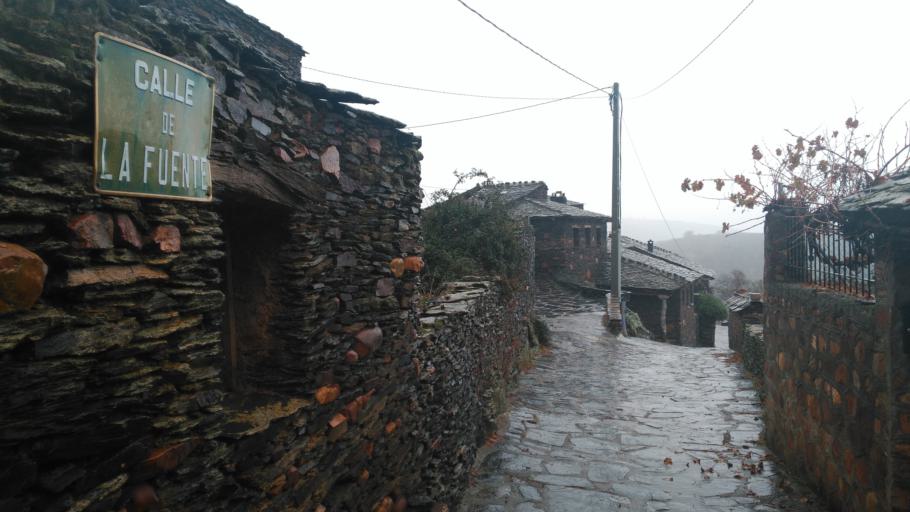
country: ES
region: Castille-La Mancha
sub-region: Provincia de Guadalajara
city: Campillo de Ranas
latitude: 41.0739
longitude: -3.3265
